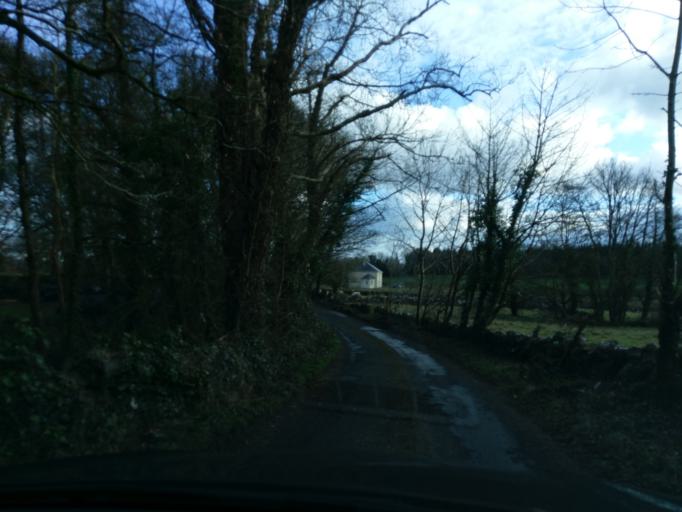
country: IE
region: Connaught
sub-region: County Galway
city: Athenry
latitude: 53.3661
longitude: -8.6499
